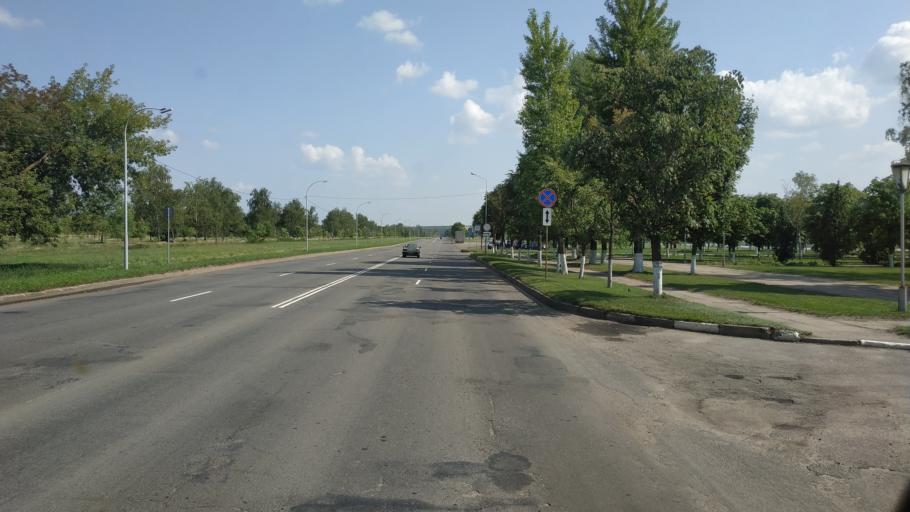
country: BY
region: Mogilev
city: Buynichy
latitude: 53.8651
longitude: 30.3174
